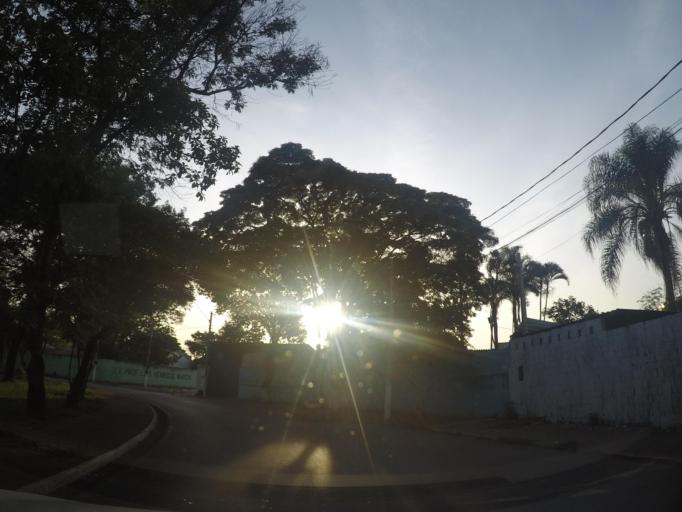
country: BR
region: Sao Paulo
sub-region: Hortolandia
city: Hortolandia
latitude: -22.8506
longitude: -47.1647
